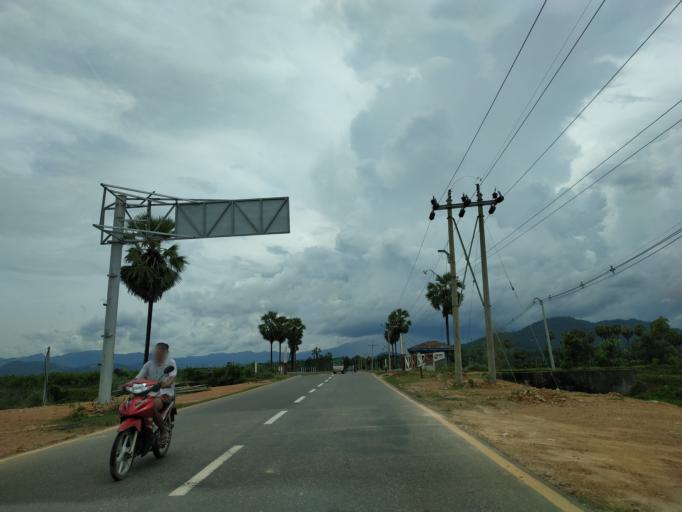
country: MM
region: Tanintharyi
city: Dawei
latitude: 14.0718
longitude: 98.2120
